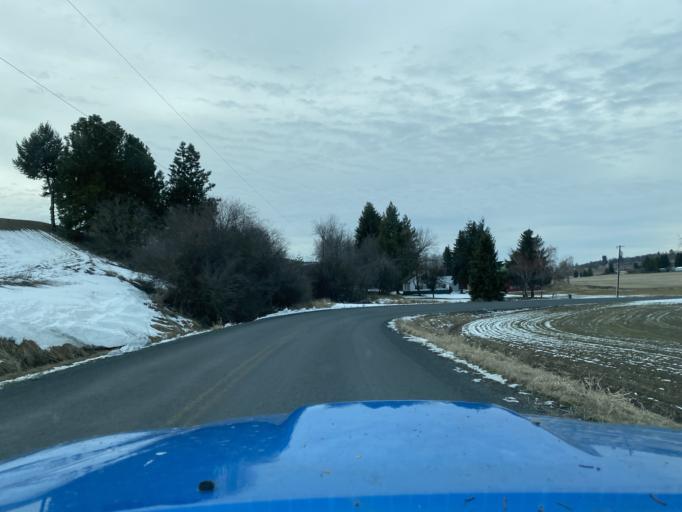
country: US
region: Idaho
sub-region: Latah County
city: Moscow
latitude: 46.7120
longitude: -116.9578
